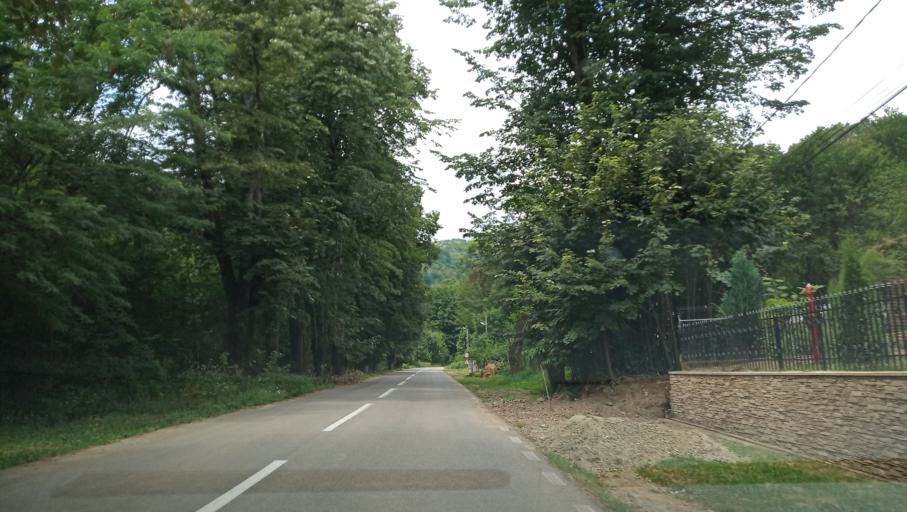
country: RO
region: Gorj
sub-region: Comuna Tismana
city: Pocruia
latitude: 45.0707
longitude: 22.9368
